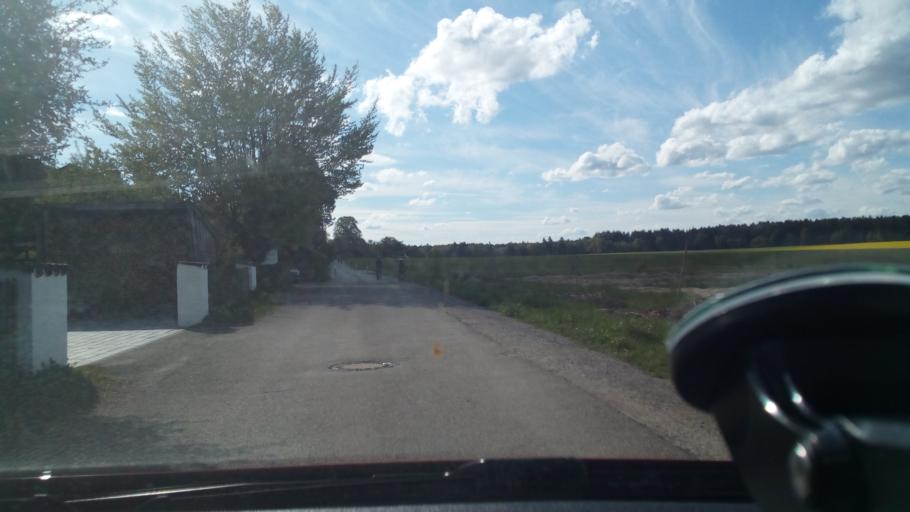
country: DE
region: Bavaria
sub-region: Upper Bavaria
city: Holzkirchen
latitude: 47.8816
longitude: 11.6781
